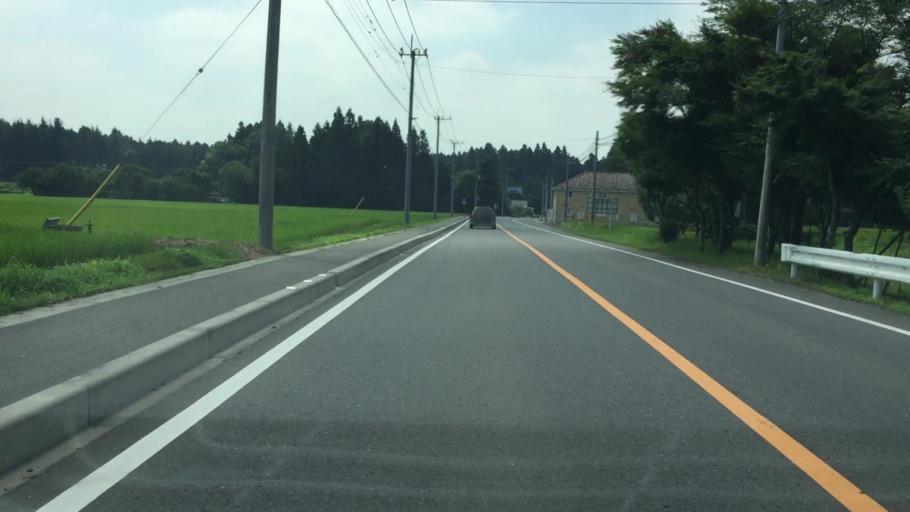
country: JP
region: Tochigi
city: Kuroiso
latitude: 36.9387
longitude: 139.9621
